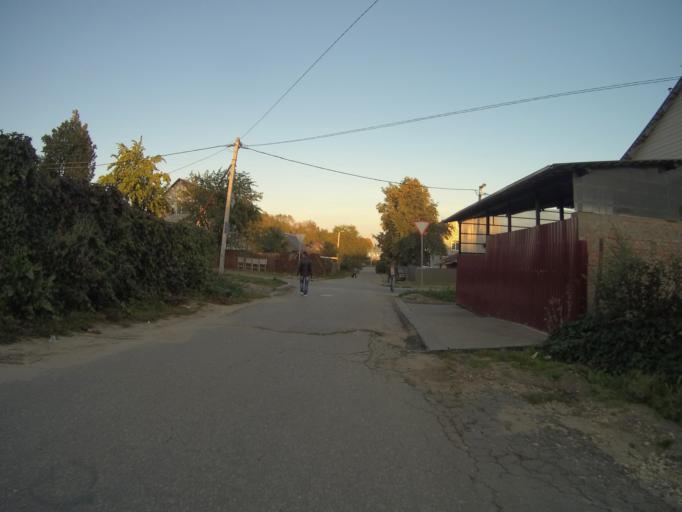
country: RU
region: Vladimir
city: Vladimir
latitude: 56.1143
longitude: 40.3659
